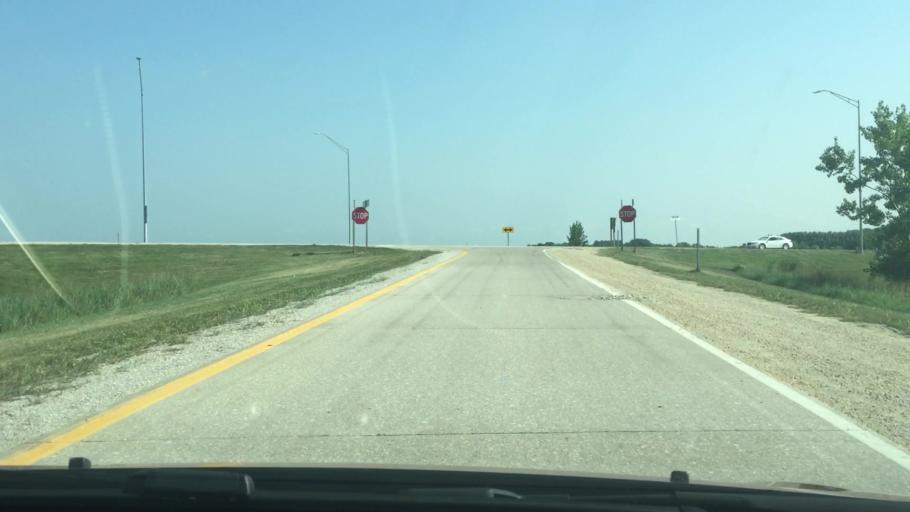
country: US
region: Iowa
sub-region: Scott County
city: Blue Grass
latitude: 41.5115
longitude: -90.7559
